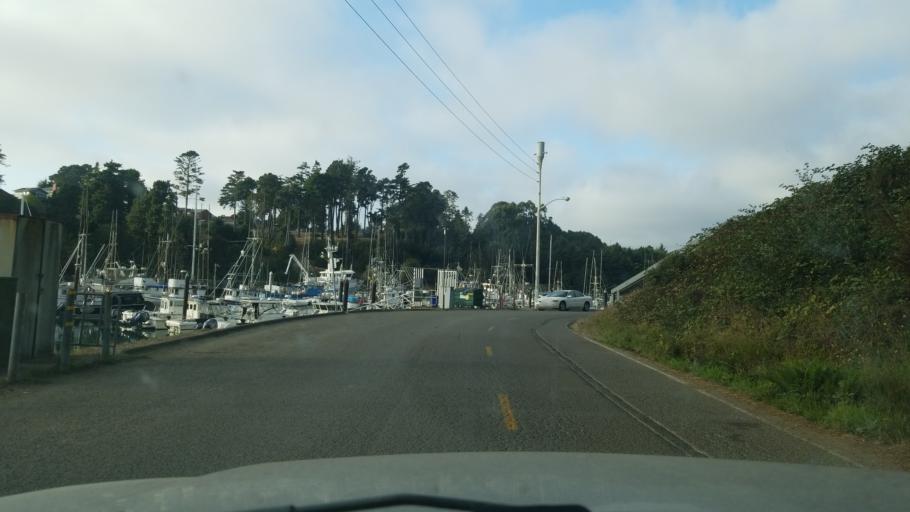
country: US
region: California
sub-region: Mendocino County
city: Fort Bragg
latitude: 39.4237
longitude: -123.8008
